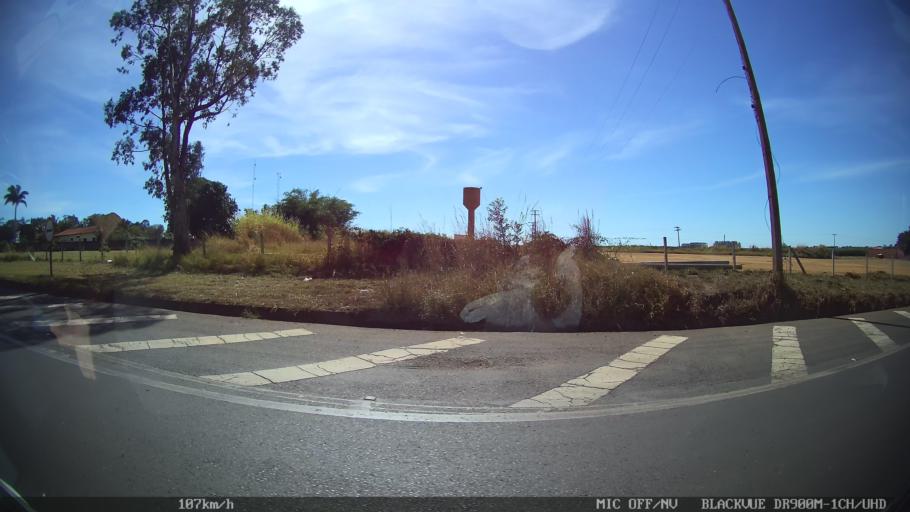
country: BR
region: Sao Paulo
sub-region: Franca
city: Franca
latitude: -20.5561
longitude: -47.5679
